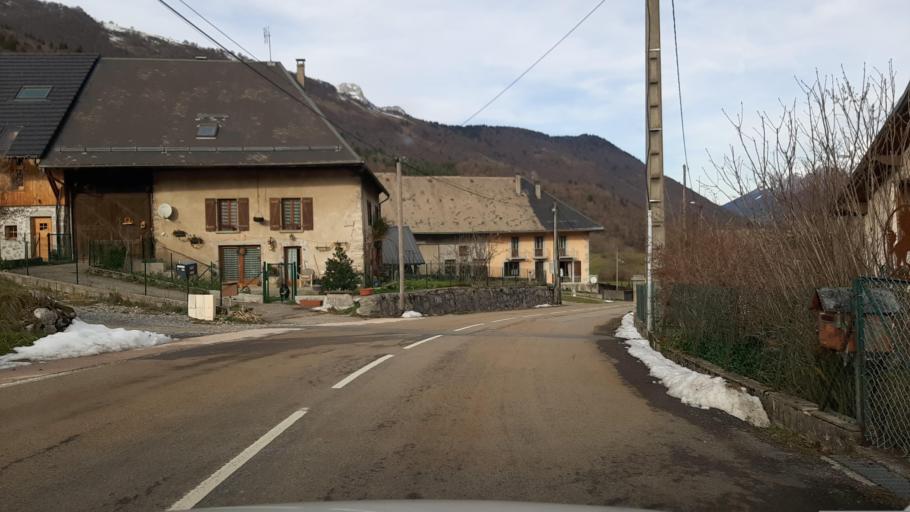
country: FR
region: Rhone-Alpes
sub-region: Departement de la Savoie
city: Coise-Saint-Jean-Pied-Gauthier
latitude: 45.5967
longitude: 6.1368
